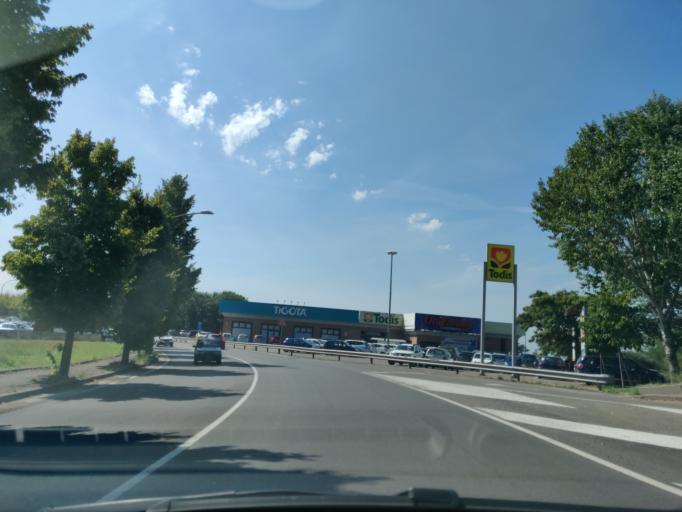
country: IT
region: Latium
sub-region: Provincia di Viterbo
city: Viterbo
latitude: 42.4242
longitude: 12.0936
